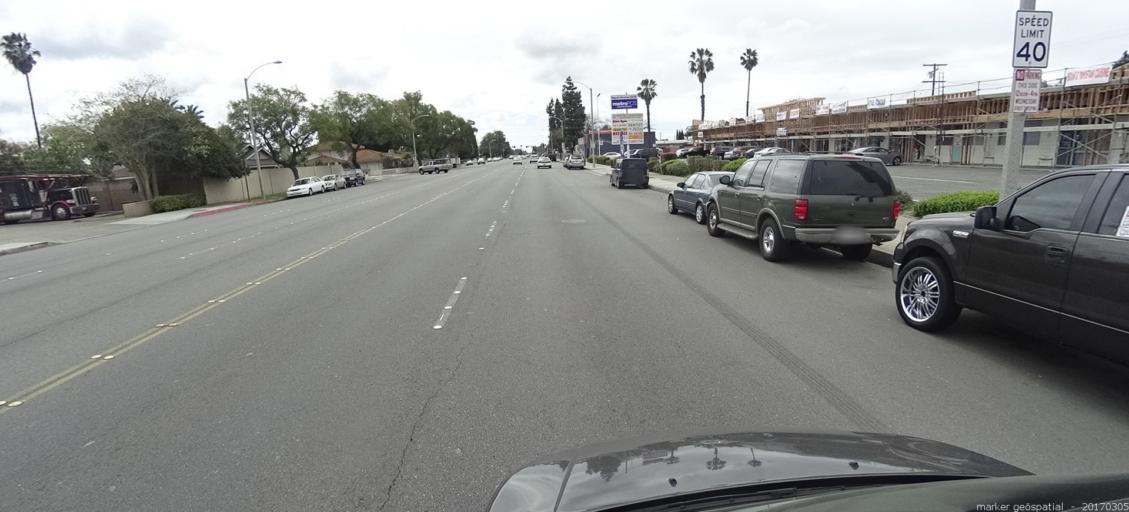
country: US
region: California
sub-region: Orange County
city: Stanton
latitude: 33.8282
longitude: -117.9761
